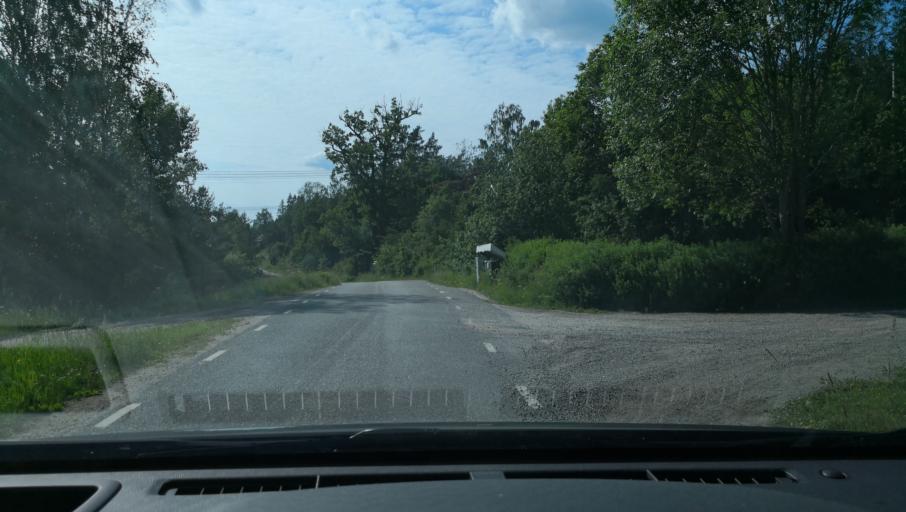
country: SE
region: Uppsala
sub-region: Enkopings Kommun
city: Orsundsbro
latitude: 59.8416
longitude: 17.1962
